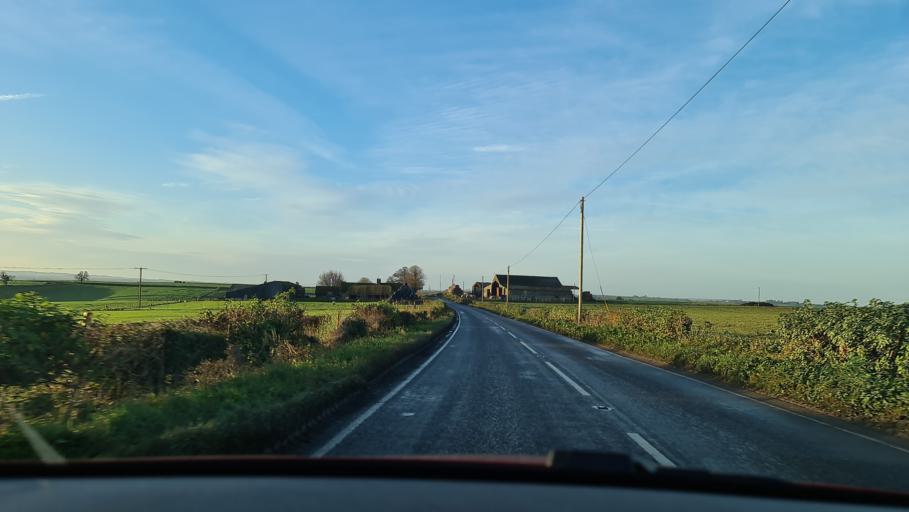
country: GB
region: England
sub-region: Buckinghamshire
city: Waddesdon
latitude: 51.8199
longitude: -0.9238
